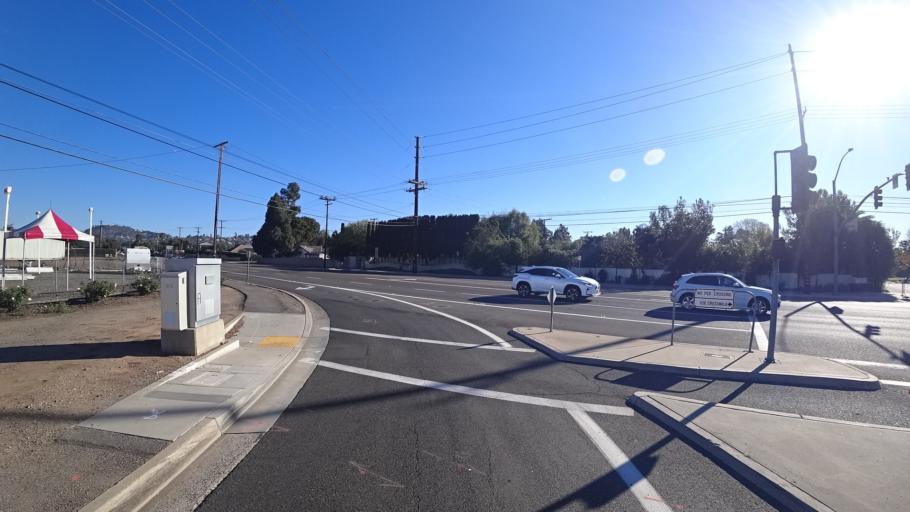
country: US
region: California
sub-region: Orange County
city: North Tustin
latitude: 33.7590
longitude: -117.8020
